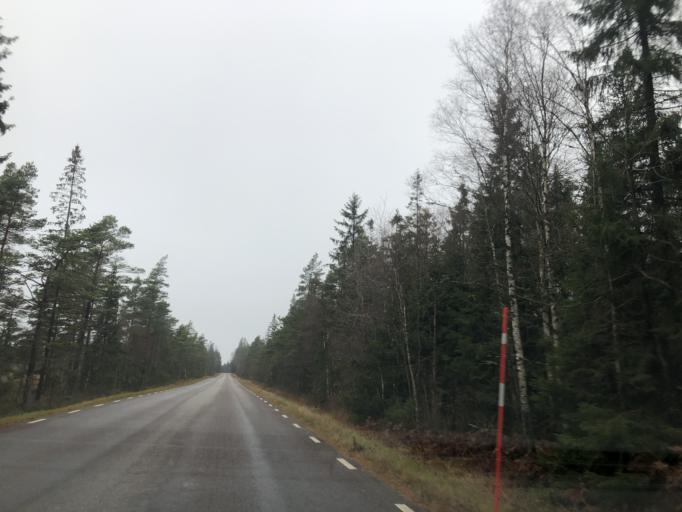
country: SE
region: Vaestra Goetaland
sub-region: Ulricehamns Kommun
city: Ulricehamn
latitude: 57.7583
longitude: 13.4963
